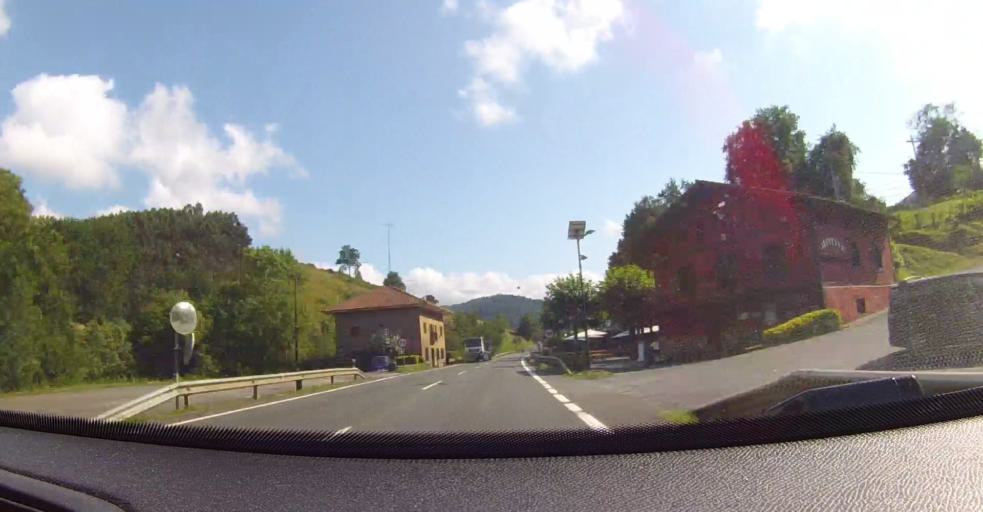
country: ES
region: Basque Country
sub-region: Bizkaia
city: Muxika
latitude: 43.2767
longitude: -2.6847
